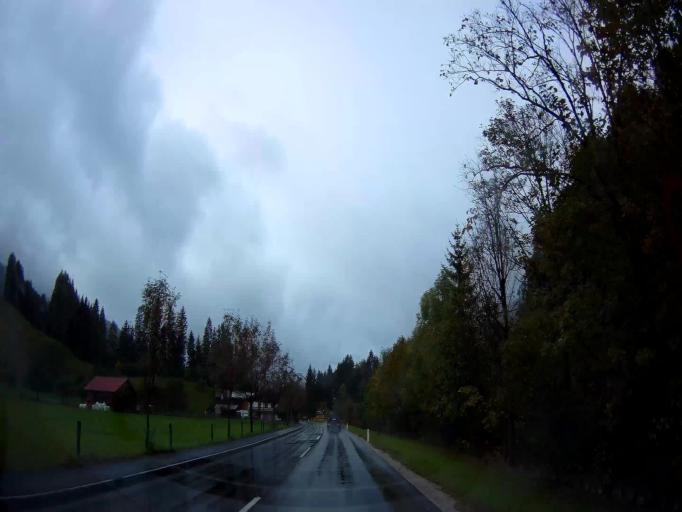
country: AT
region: Salzburg
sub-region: Politischer Bezirk Zell am See
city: Leogang
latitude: 47.4396
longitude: 12.7508
